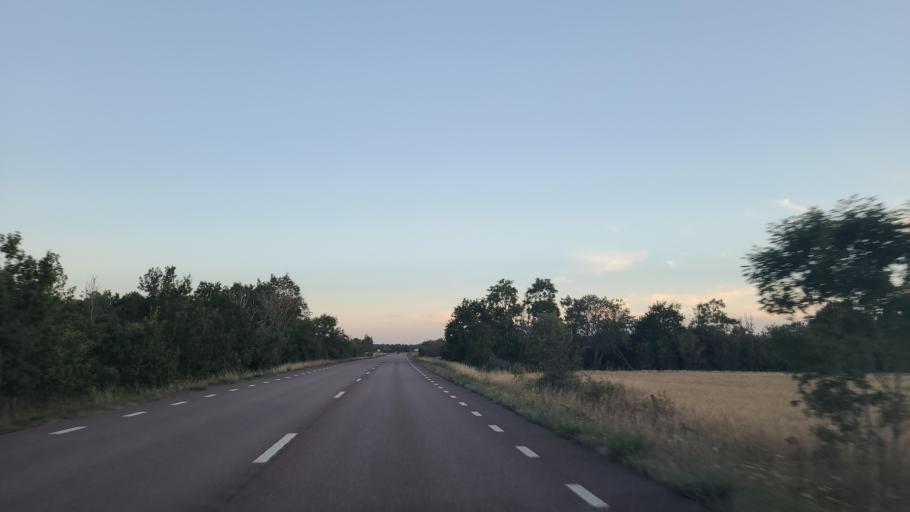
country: SE
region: Kalmar
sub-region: Borgholms Kommun
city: Borgholm
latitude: 57.0360
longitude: 16.8675
